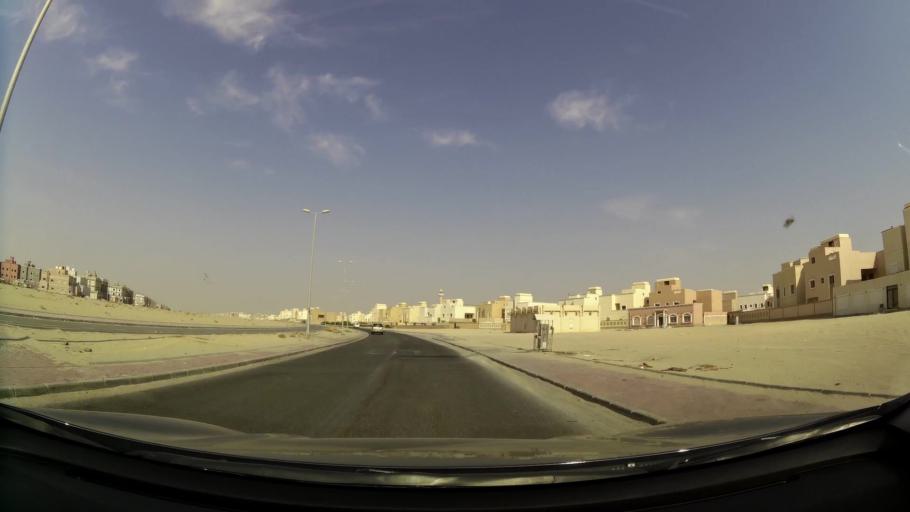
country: KW
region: Al Ahmadi
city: Al Wafrah
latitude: 28.7951
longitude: 48.0651
